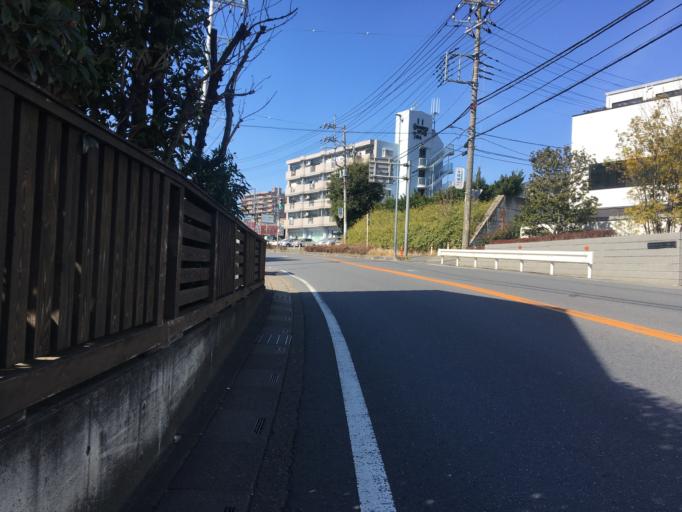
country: JP
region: Saitama
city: Asaka
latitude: 35.7985
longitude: 139.5778
